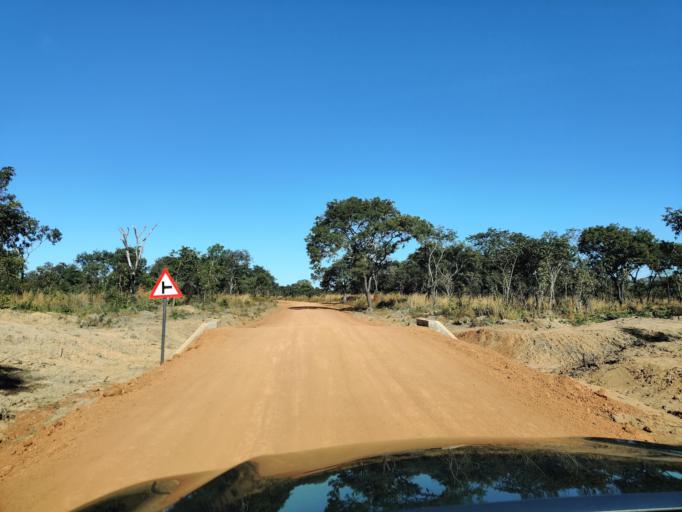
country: ZM
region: Central
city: Mkushi
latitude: -13.5543
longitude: 29.3298
